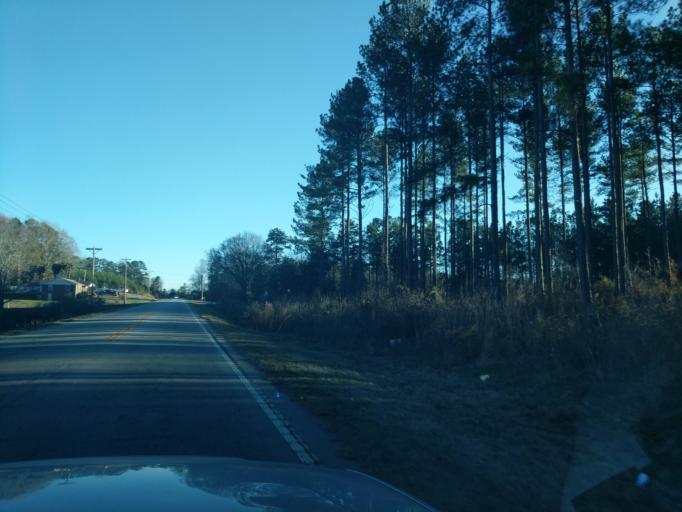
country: US
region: South Carolina
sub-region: Oconee County
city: Westminster
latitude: 34.6431
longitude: -83.0654
